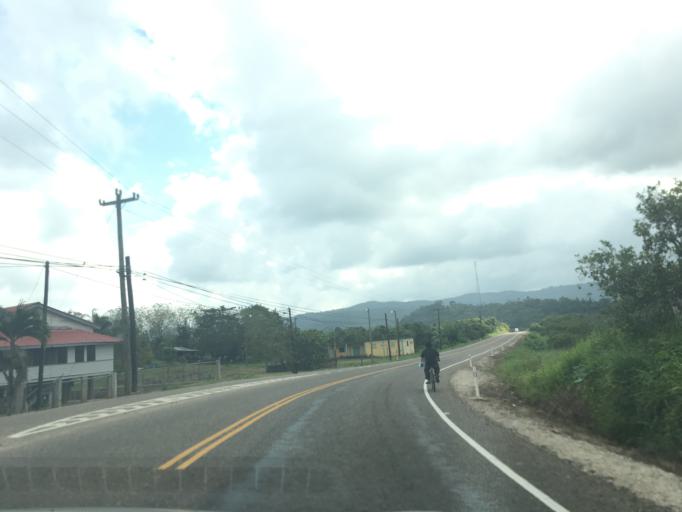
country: BZ
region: Stann Creek
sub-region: Dangriga
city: Dangriga
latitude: 16.9973
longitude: -88.4079
